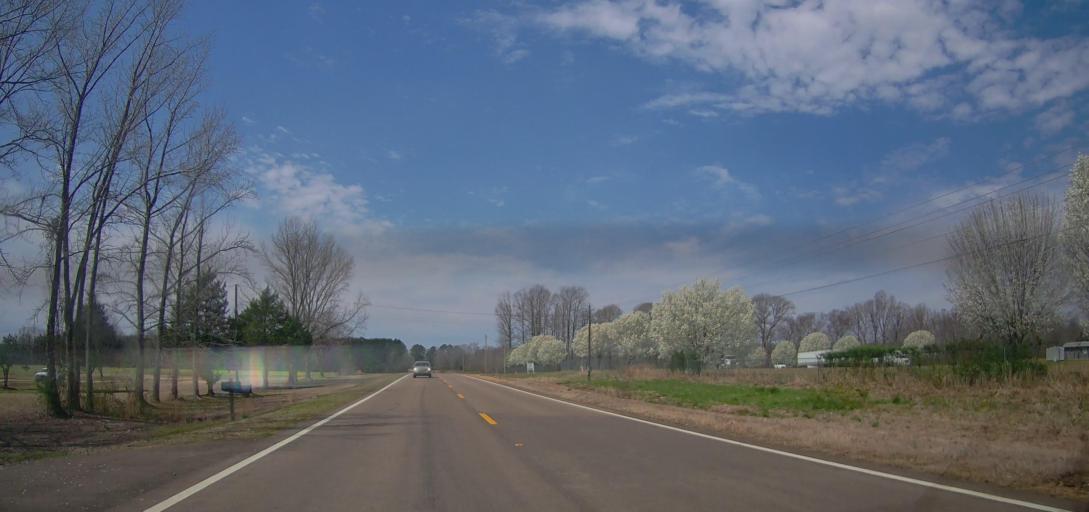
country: US
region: Mississippi
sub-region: Union County
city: New Albany
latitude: 34.6164
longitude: -89.1694
